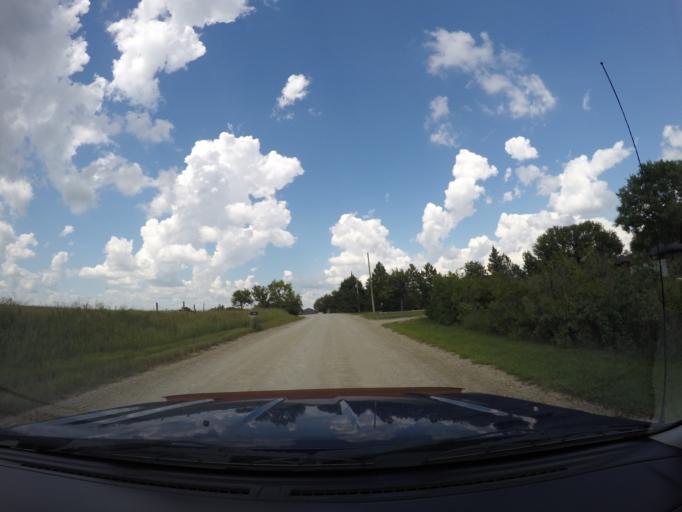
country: US
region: Kansas
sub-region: Wabaunsee County
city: Alma
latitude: 39.0231
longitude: -96.2935
